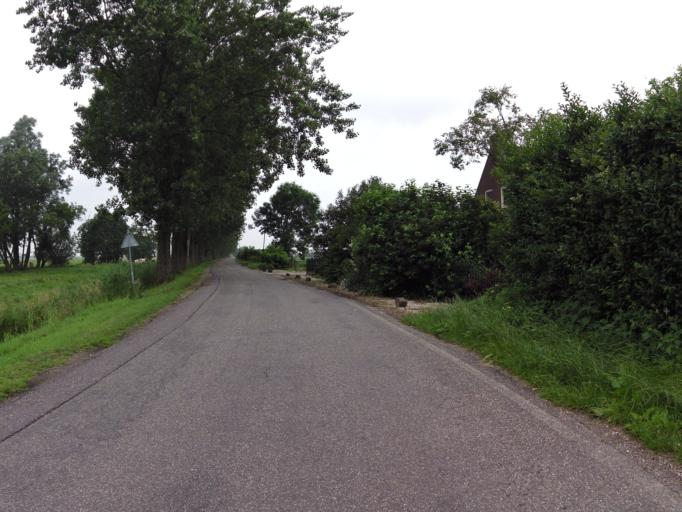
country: NL
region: Utrecht
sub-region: Stichtse Vecht
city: Spechtenkamp
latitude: 52.1234
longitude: 4.9693
